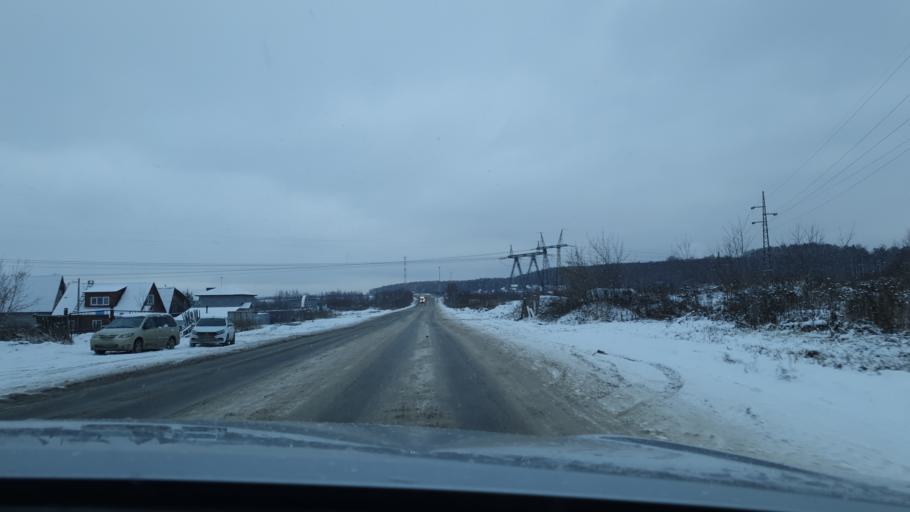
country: RU
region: Sverdlovsk
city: Istok
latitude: 56.7751
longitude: 60.7386
